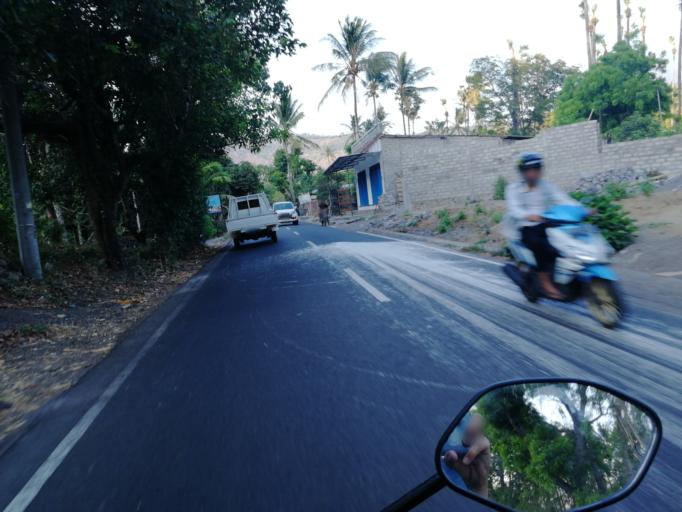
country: ID
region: Bali
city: Banjar Buayang
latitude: -8.3401
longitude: 115.6199
